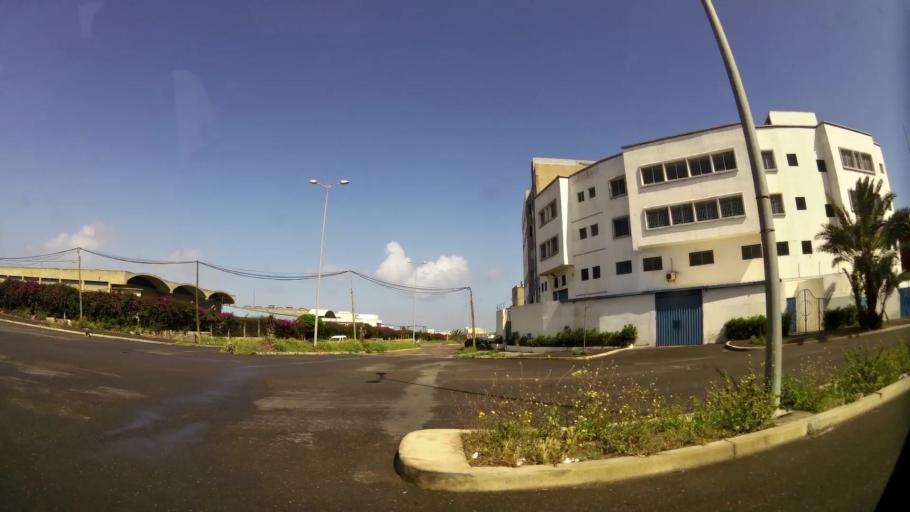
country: MA
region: Grand Casablanca
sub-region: Mediouna
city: Tit Mellil
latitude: 33.6170
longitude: -7.5083
